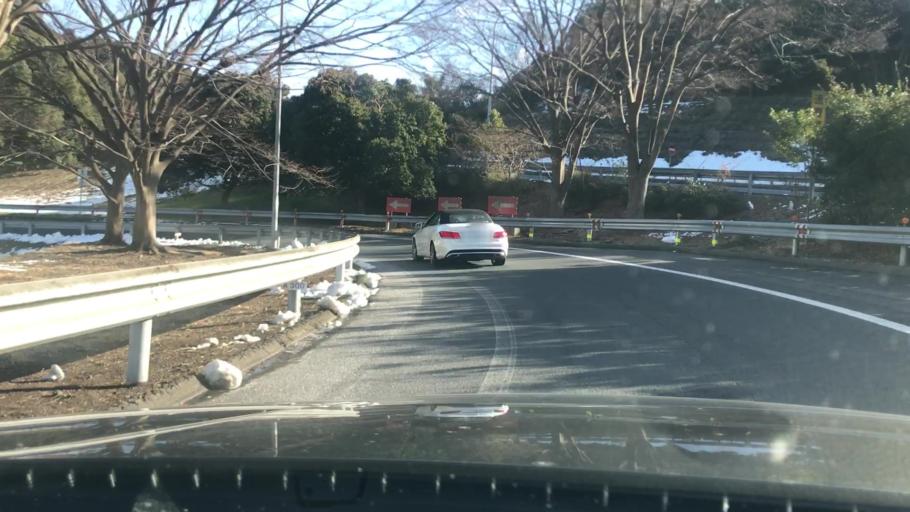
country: JP
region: Kanagawa
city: Zushi
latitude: 35.2925
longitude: 139.6181
